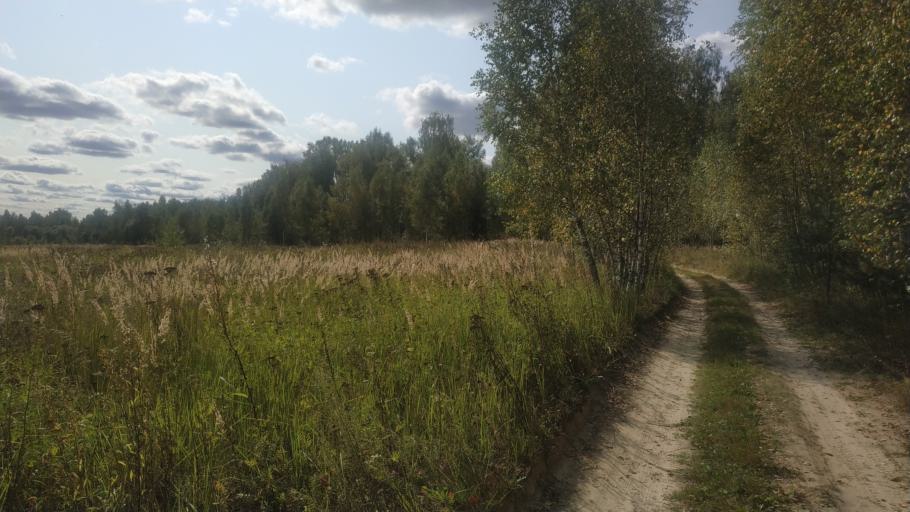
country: RU
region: Brjansk
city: Zhukovka
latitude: 53.5354
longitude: 33.6627
